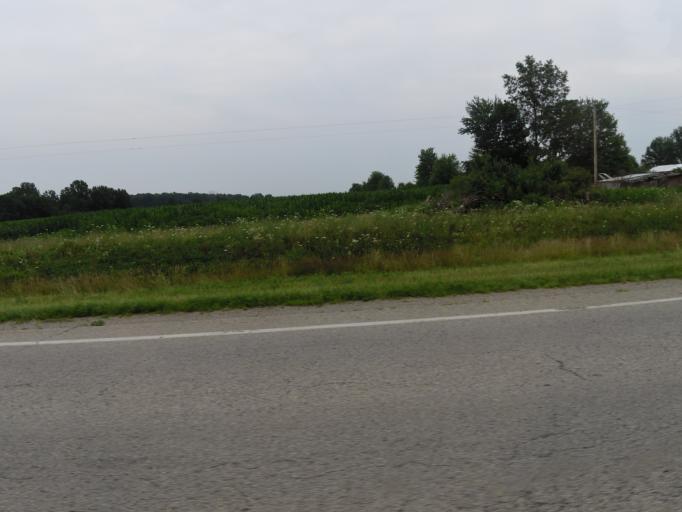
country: US
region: Ohio
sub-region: Brown County
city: Mount Orab
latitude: 39.1217
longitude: -83.9330
